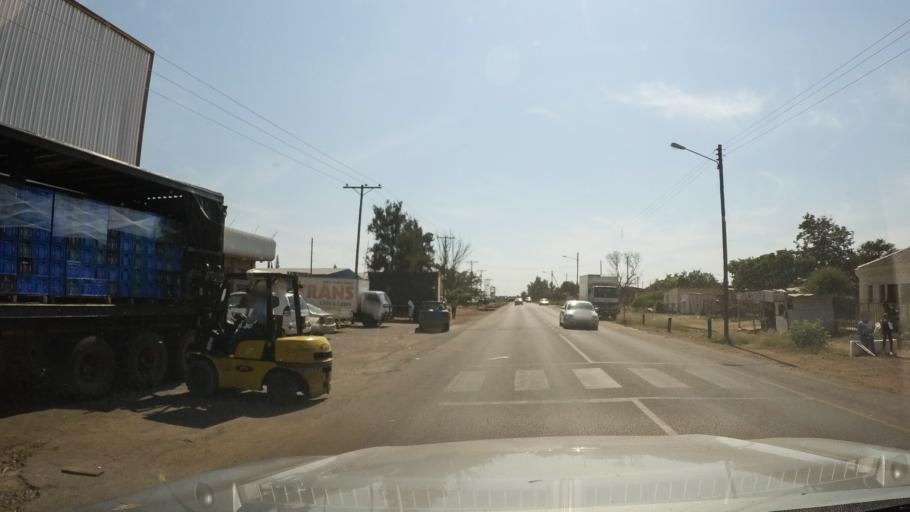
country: BW
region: South East
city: Lobatse
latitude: -25.2048
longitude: 25.6848
